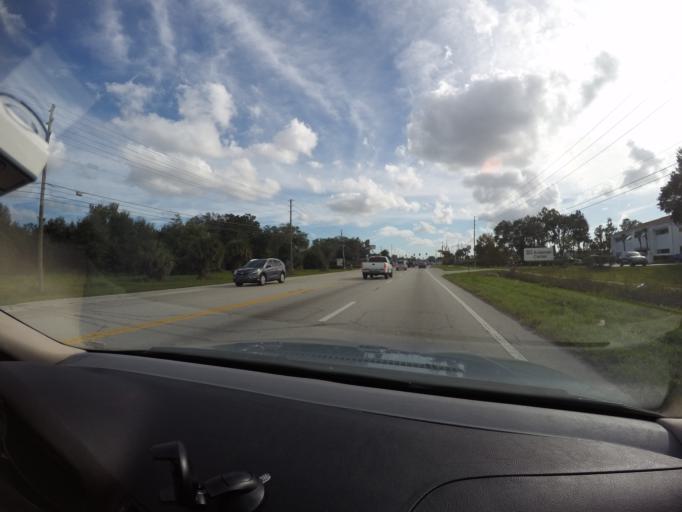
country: US
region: Florida
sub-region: Orange County
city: Belle Isle
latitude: 28.4546
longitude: -81.3646
